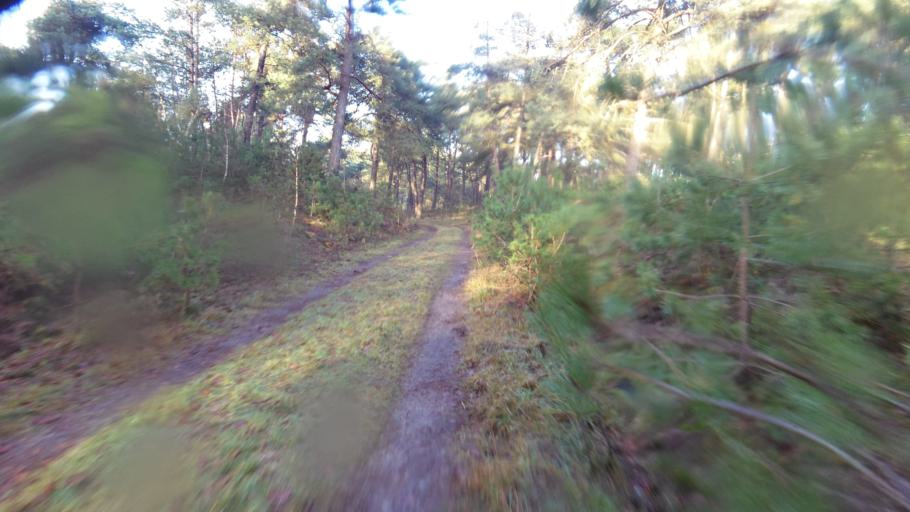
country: NL
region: Gelderland
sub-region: Gemeente Barneveld
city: Garderen
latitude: 52.2009
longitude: 5.7397
